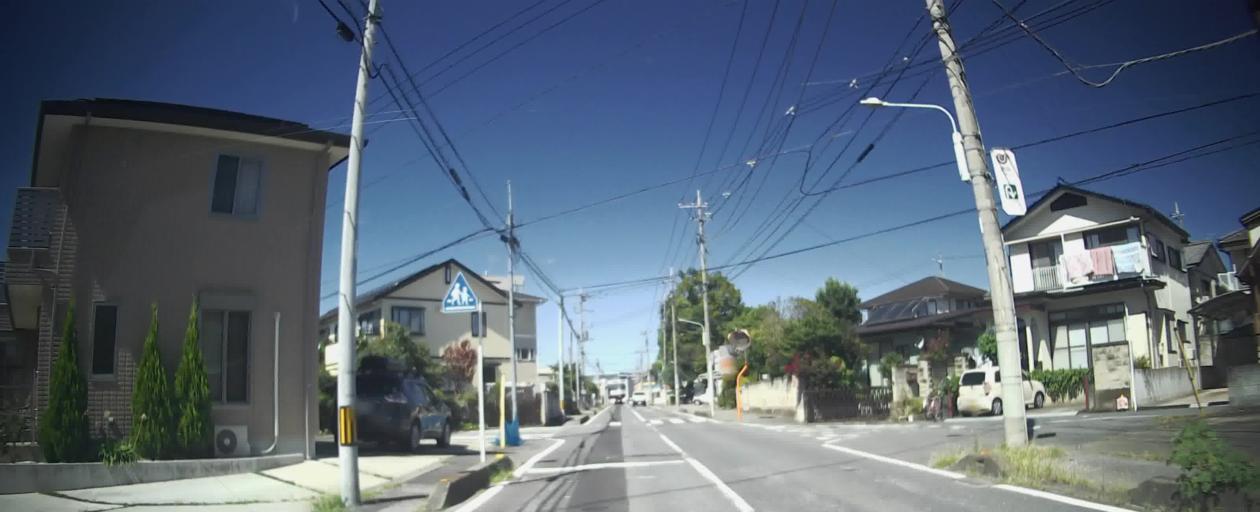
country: JP
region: Gunma
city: Maebashi-shi
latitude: 36.3991
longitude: 139.0573
